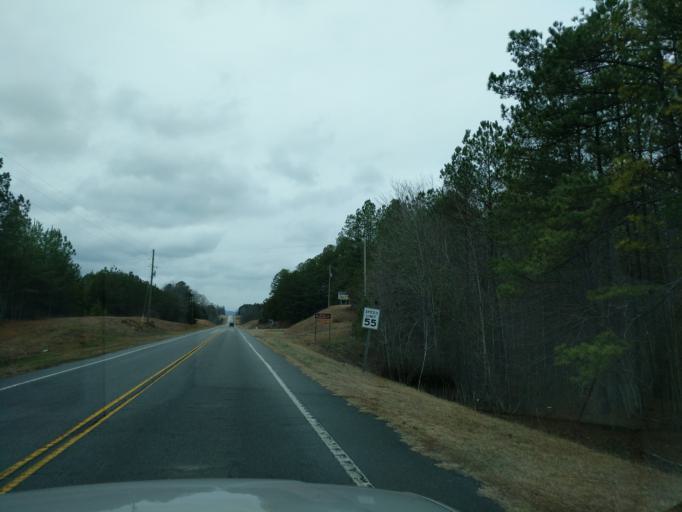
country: US
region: South Carolina
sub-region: Oconee County
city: Walhalla
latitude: 34.9095
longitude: -82.9608
